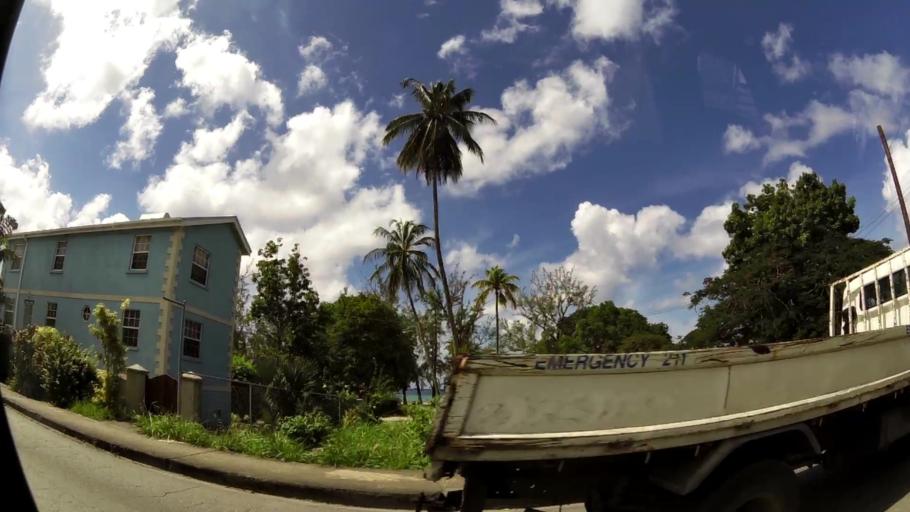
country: BB
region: Saint James
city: Holetown
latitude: 13.1449
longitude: -59.6381
